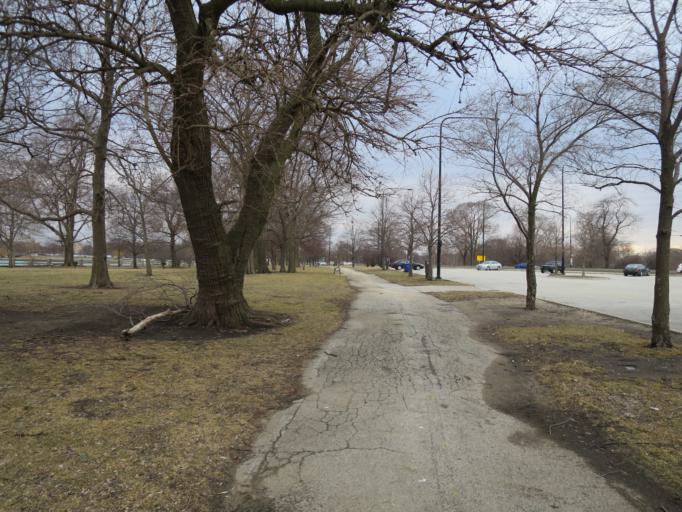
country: US
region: Illinois
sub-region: Cook County
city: Chicago
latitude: 41.7805
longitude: -87.5736
